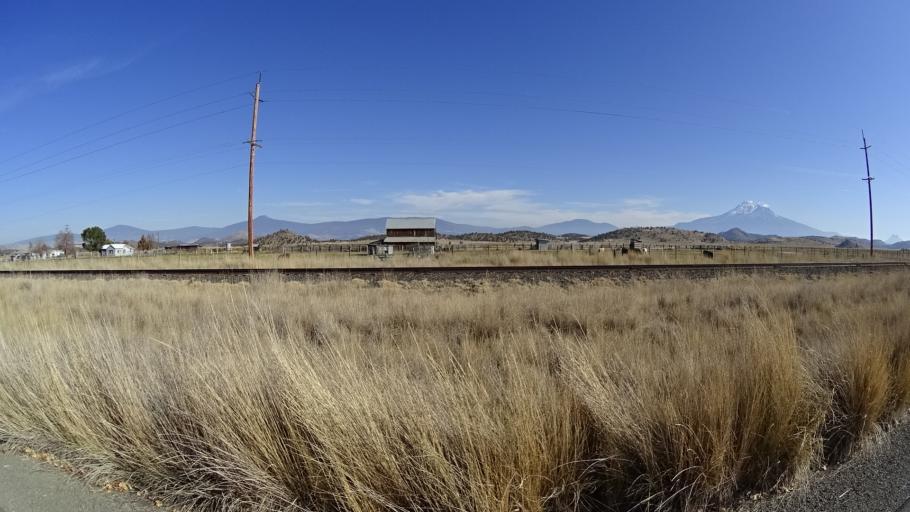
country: US
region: California
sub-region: Siskiyou County
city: Montague
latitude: 41.6313
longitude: -122.5220
